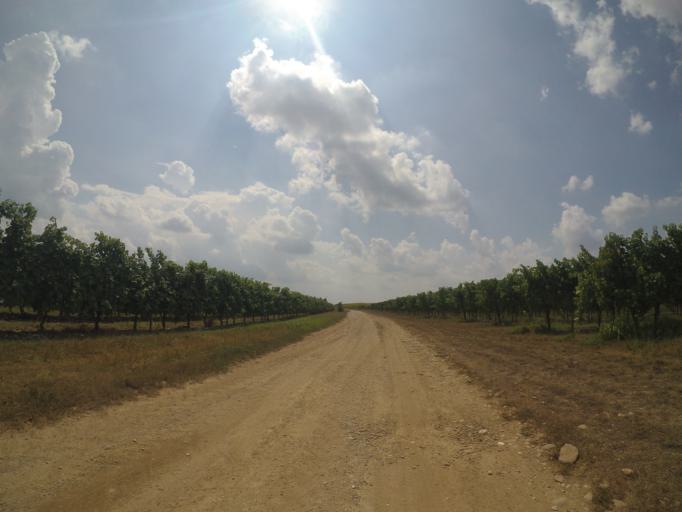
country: IT
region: Friuli Venezia Giulia
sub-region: Provincia di Udine
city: Bertiolo
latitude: 45.9549
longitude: 13.0472
